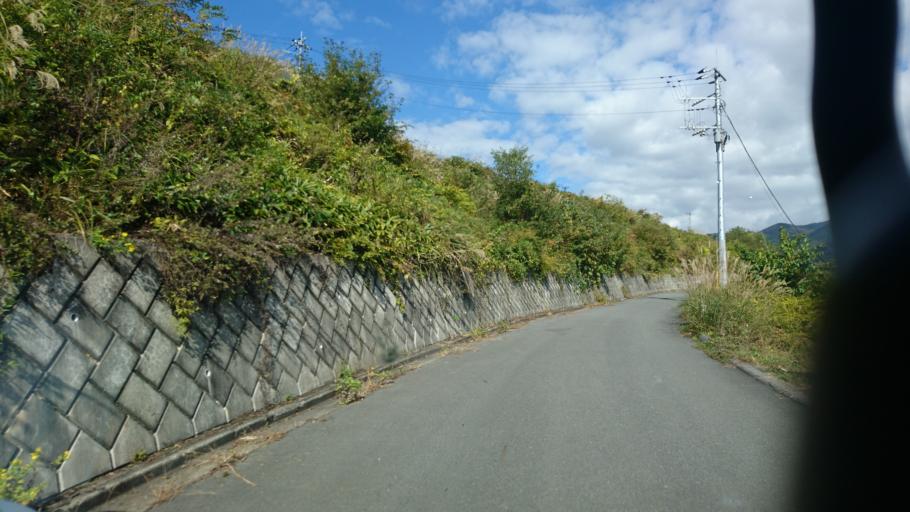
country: JP
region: Gunma
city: Omamacho-omama
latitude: 36.6084
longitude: 139.2458
